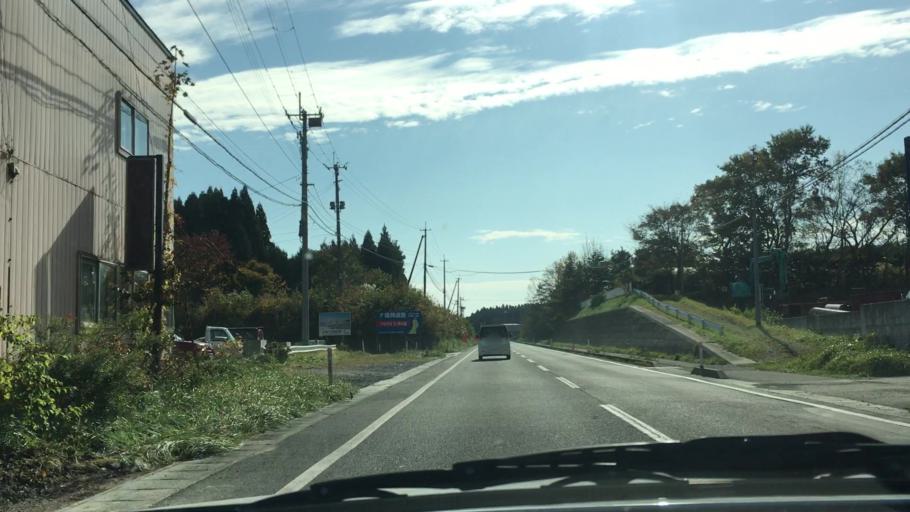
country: JP
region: Aomori
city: Hachinohe
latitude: 40.4310
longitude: 141.6902
